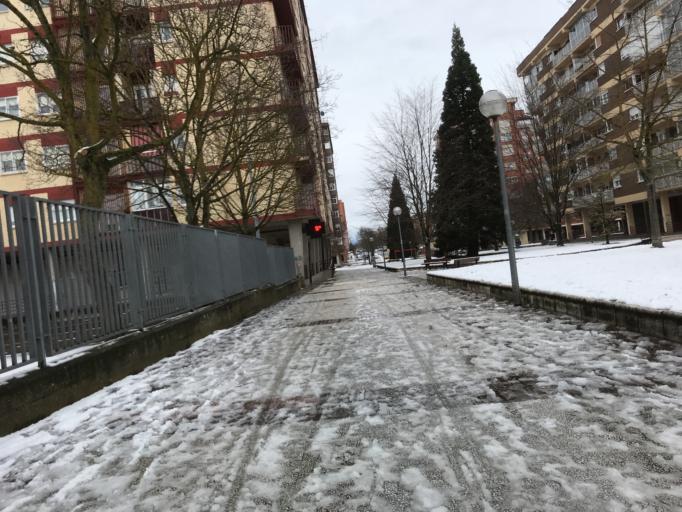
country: ES
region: Basque Country
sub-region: Provincia de Alava
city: Gasteiz / Vitoria
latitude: 42.8579
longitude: -2.6946
